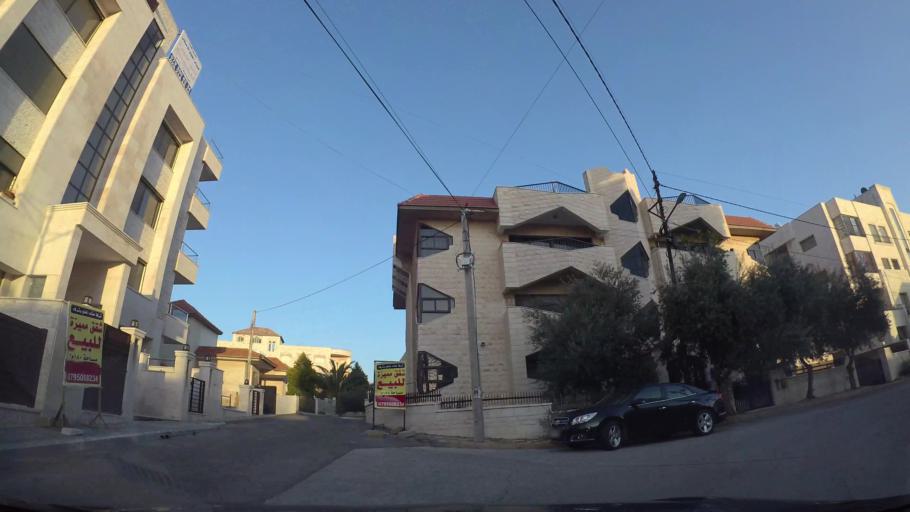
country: JO
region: Amman
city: Al Jubayhah
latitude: 31.9936
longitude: 35.8754
